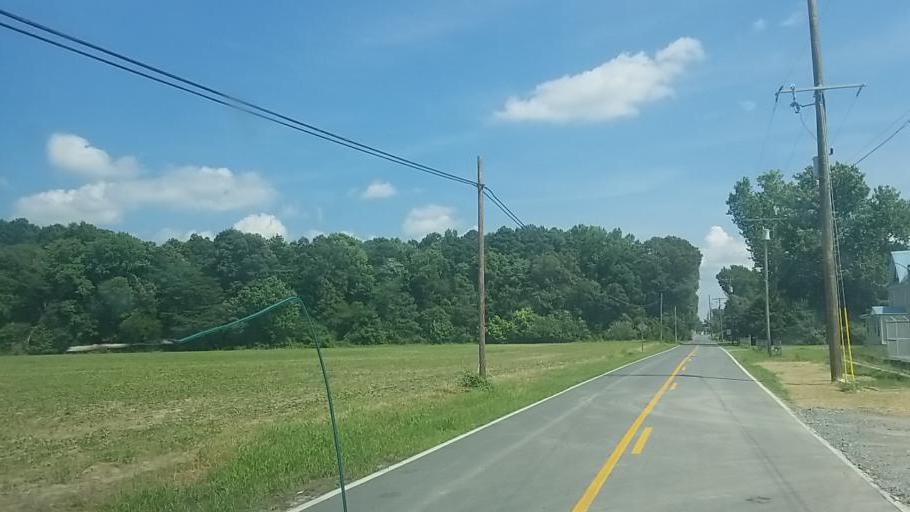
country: US
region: Maryland
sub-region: Wicomico County
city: Hebron
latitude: 38.4244
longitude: -75.6969
